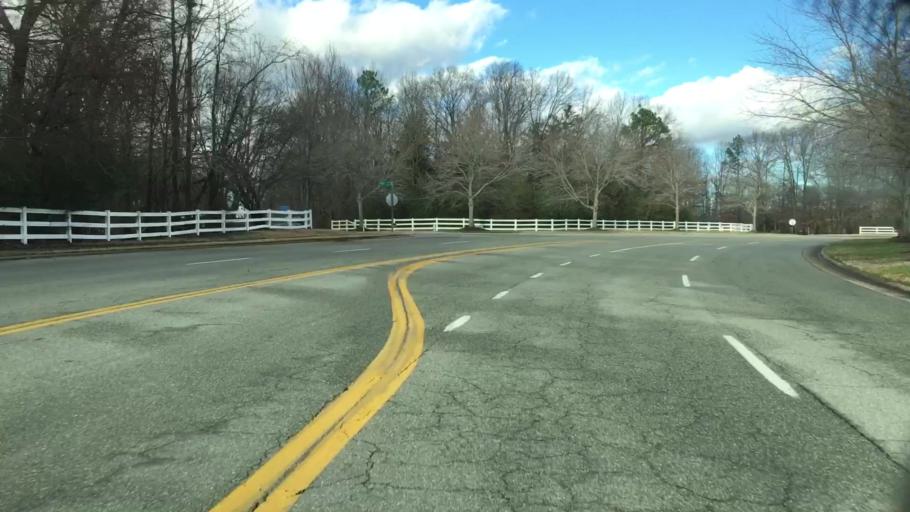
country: US
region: Virginia
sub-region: Chesterfield County
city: Bon Air
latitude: 37.5257
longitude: -77.6153
